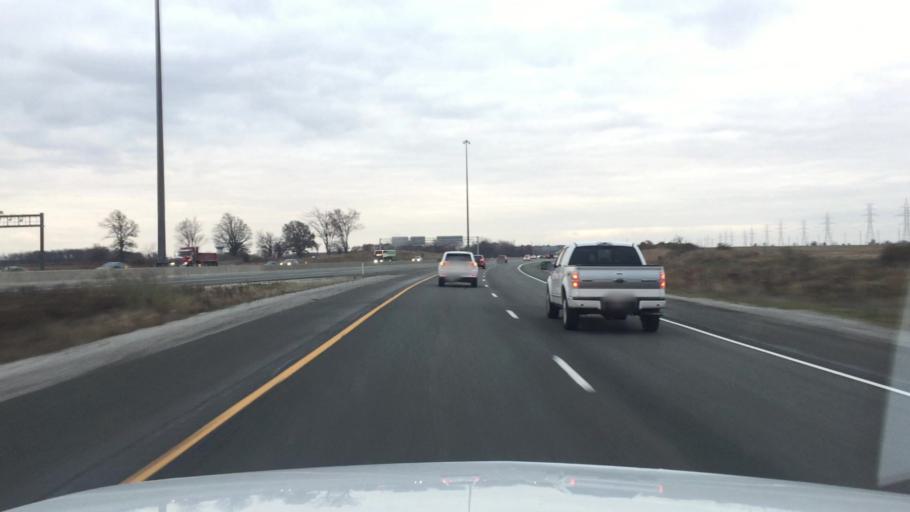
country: CA
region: Ontario
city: Oakville
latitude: 43.5220
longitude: -79.7330
